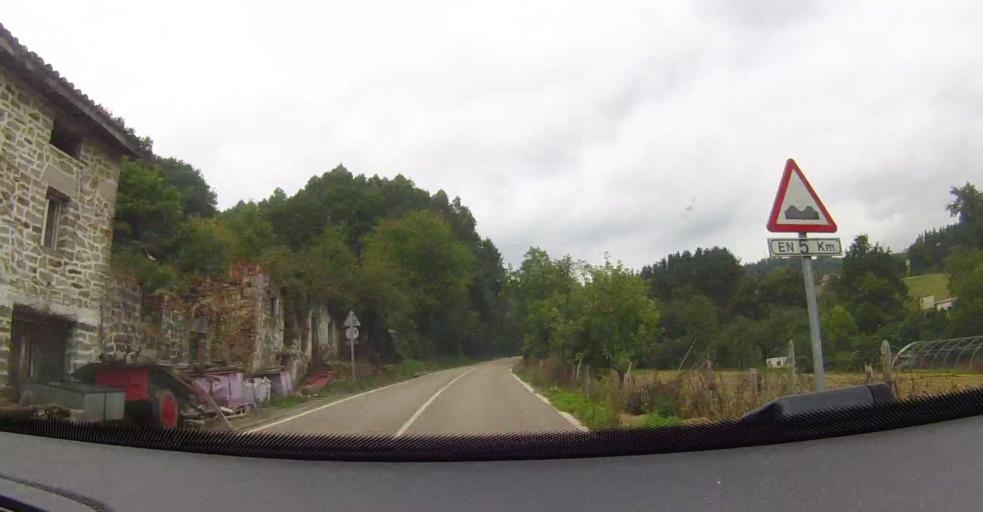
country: ES
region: Basque Country
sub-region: Bizkaia
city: Balmaseda
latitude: 43.2450
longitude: -3.2679
